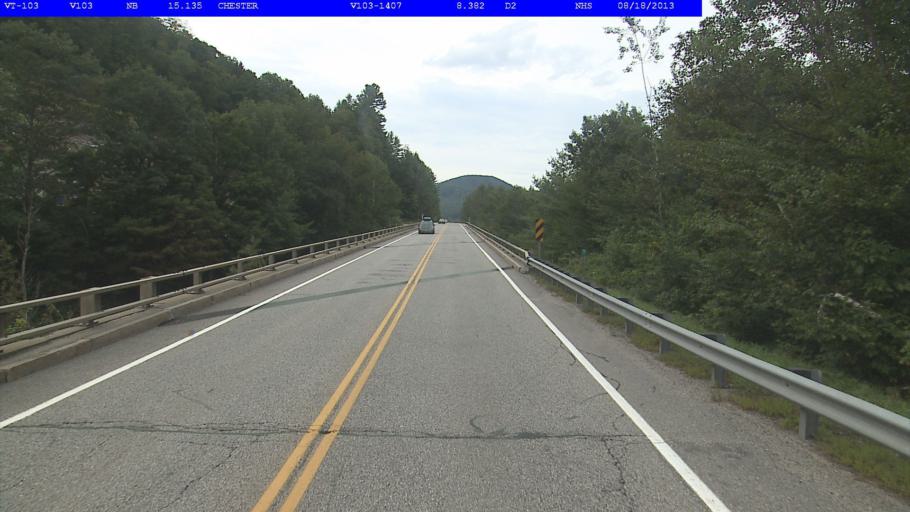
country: US
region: Vermont
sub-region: Windsor County
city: Chester
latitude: 43.3317
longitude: -72.6147
